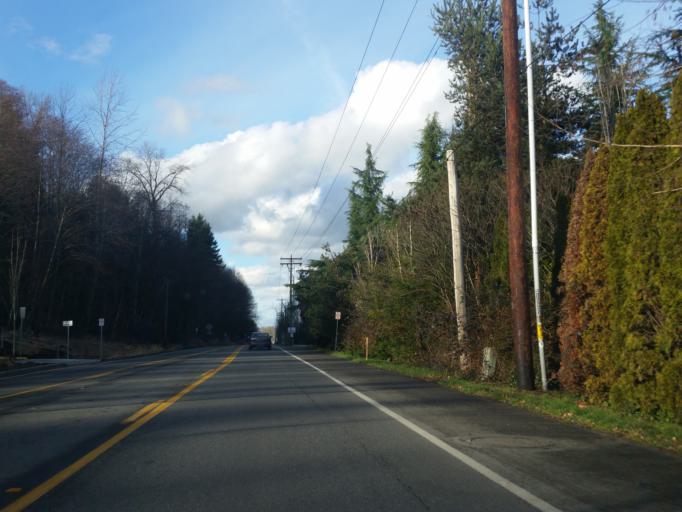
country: US
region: Washington
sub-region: King County
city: Woodinville
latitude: 47.7338
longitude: -122.1530
